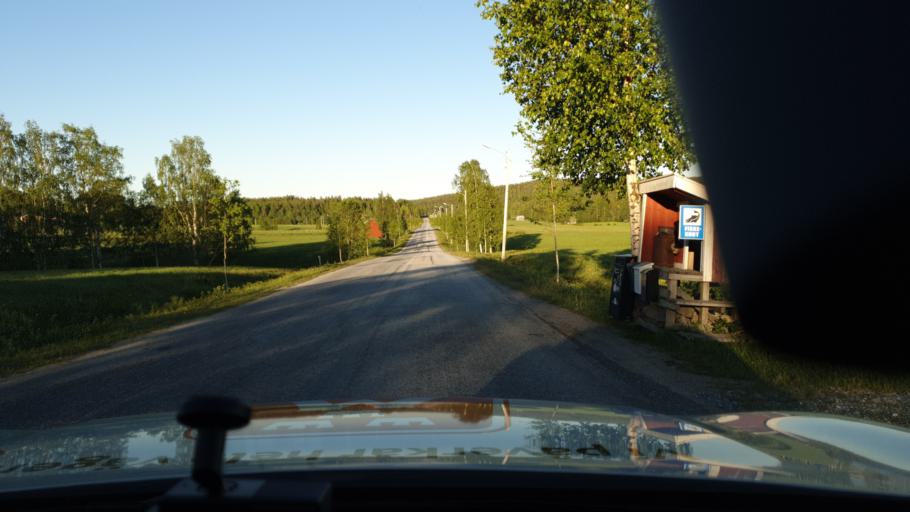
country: SE
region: Vaesterbotten
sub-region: Umea Kommun
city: Roback
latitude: 64.0130
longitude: 20.1411
